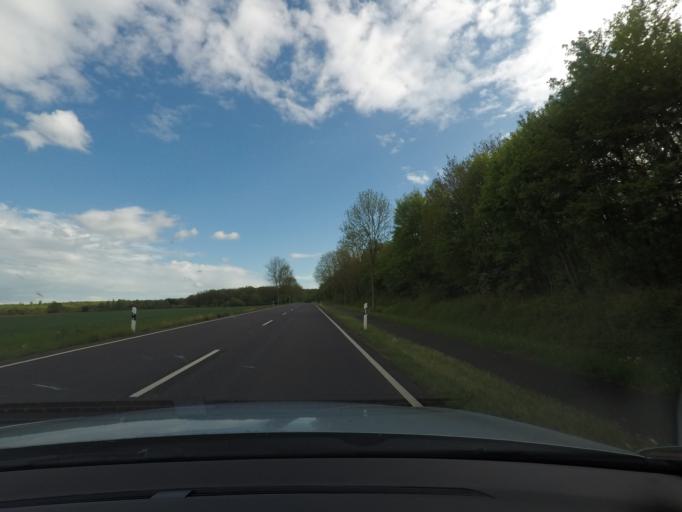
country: DE
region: Lower Saxony
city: Querenhorst
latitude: 52.3218
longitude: 10.9721
